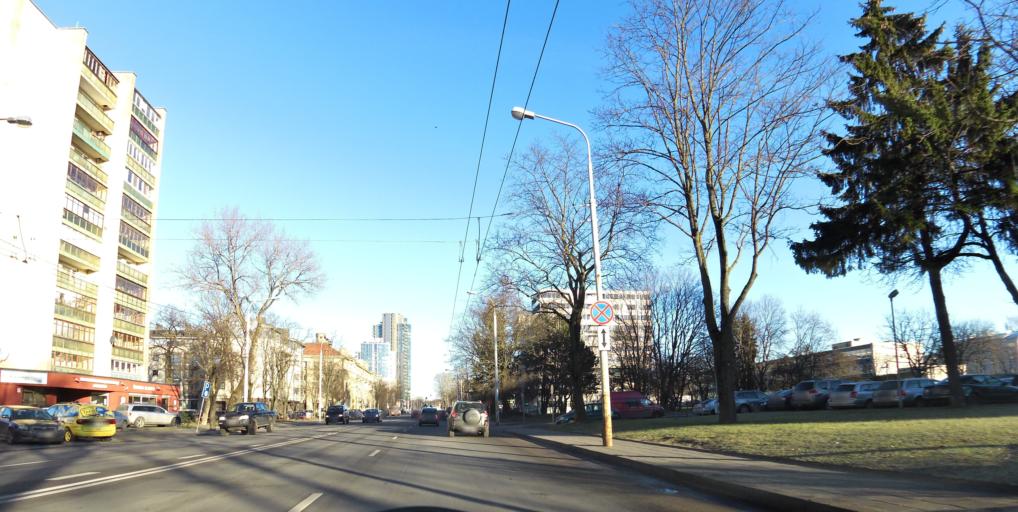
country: LT
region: Vilnius County
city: Vilkpede
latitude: 54.6760
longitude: 25.2524
